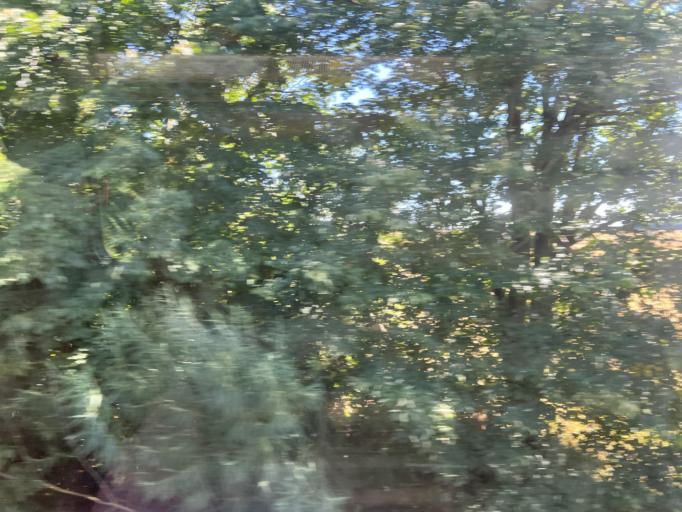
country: GB
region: England
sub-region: Lincolnshire
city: Spilsby
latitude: 53.0825
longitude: 0.0876
